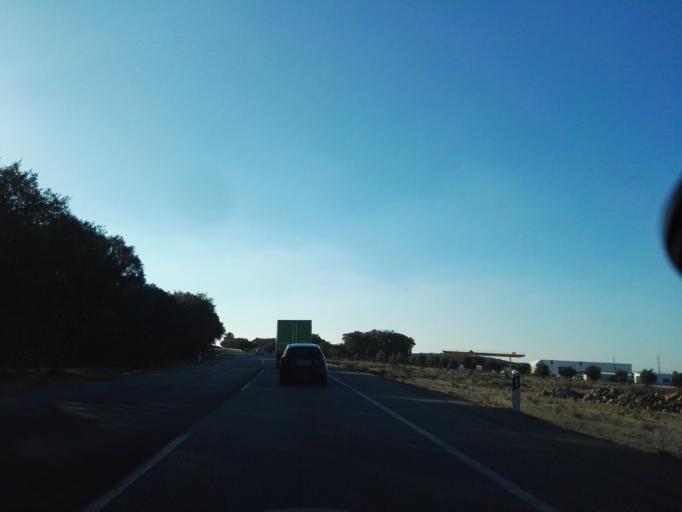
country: PT
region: Evora
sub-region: Borba
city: Borba
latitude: 38.8241
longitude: -7.5072
